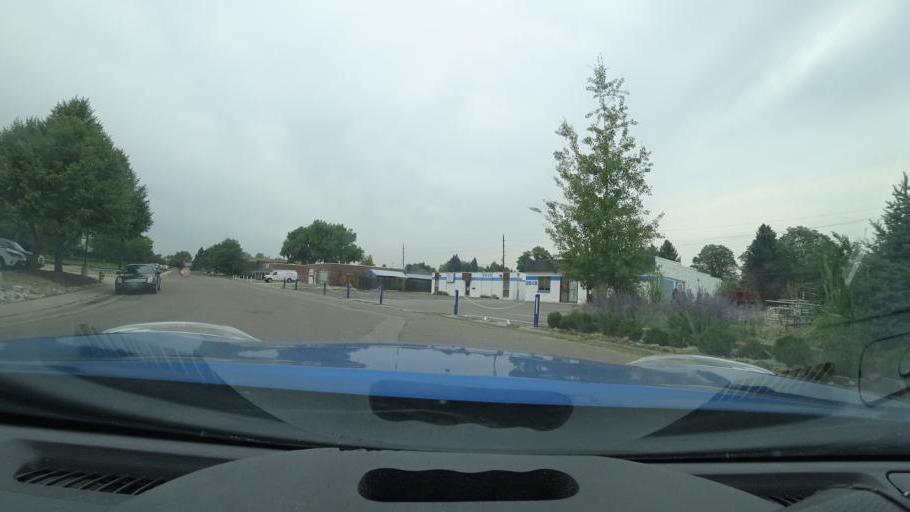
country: US
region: Colorado
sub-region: Arapahoe County
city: Glendale
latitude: 39.6797
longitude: -104.9056
